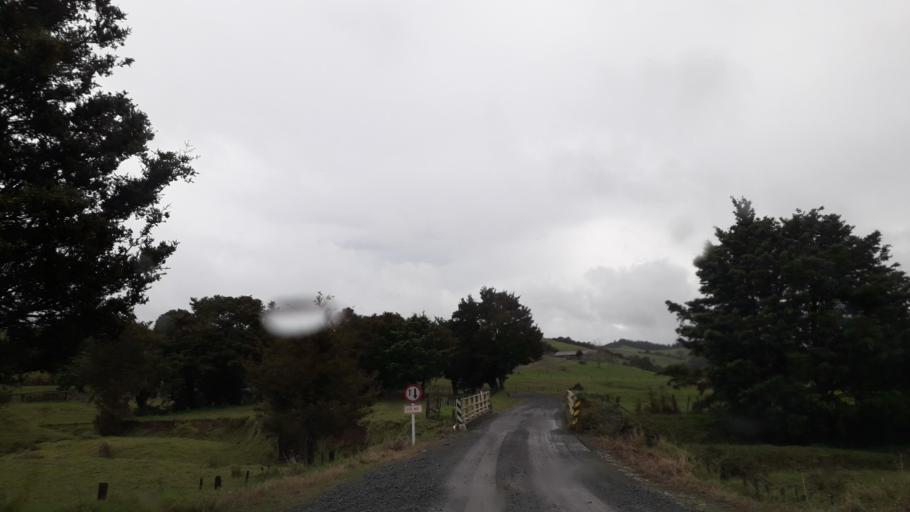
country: NZ
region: Northland
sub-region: Far North District
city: Waimate North
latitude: -35.1358
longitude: 173.7142
